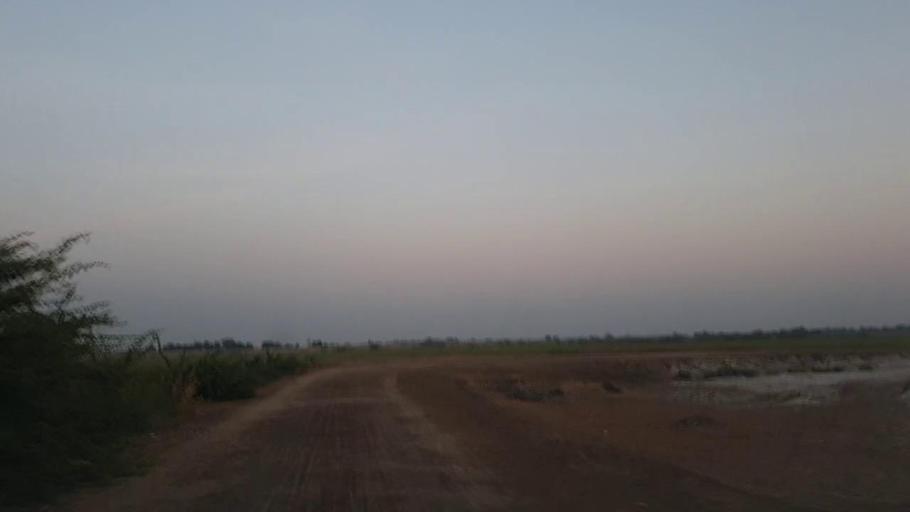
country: PK
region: Sindh
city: Naukot
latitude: 24.9966
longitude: 69.4328
